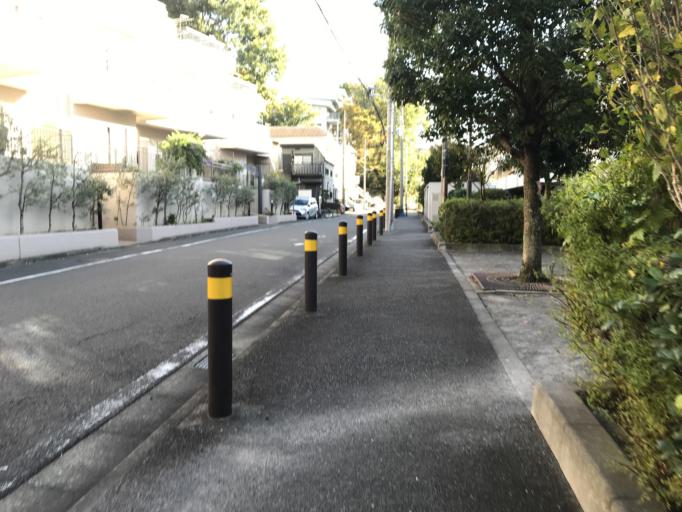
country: JP
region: Kanagawa
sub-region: Kawasaki-shi
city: Kawasaki
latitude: 35.5640
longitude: 139.6164
